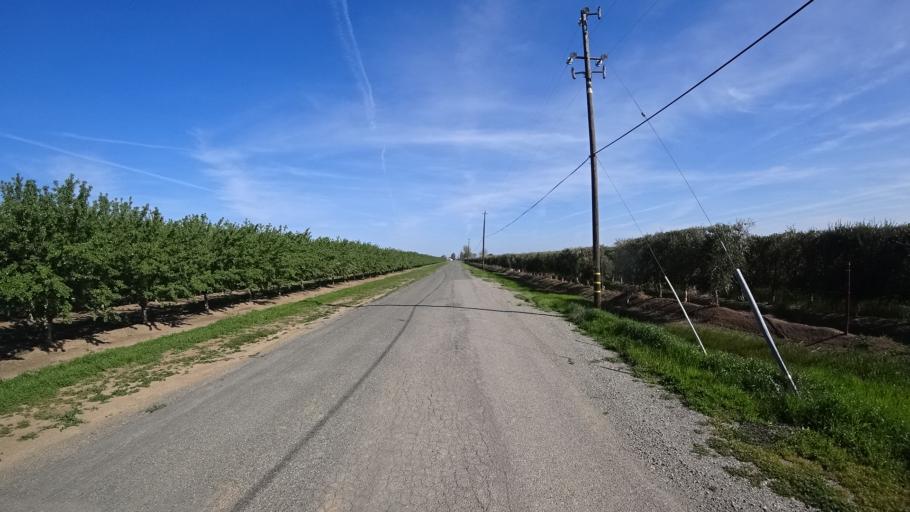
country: US
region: California
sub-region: Glenn County
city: Willows
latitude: 39.6247
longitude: -122.2161
